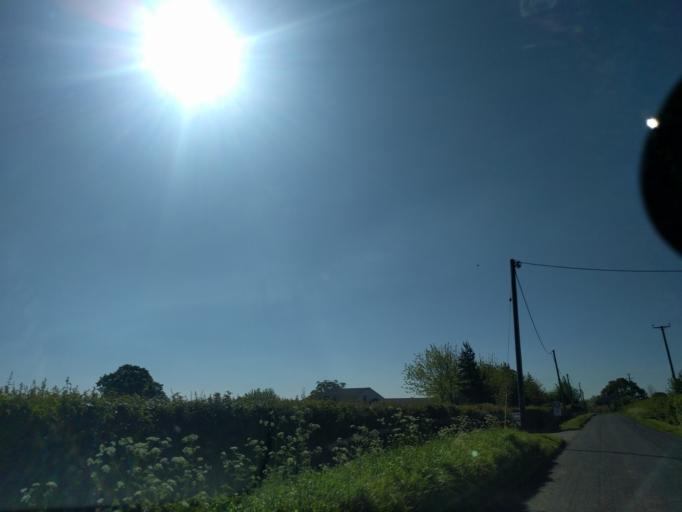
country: GB
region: England
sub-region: Wiltshire
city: Bratton
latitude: 51.2920
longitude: -2.1306
